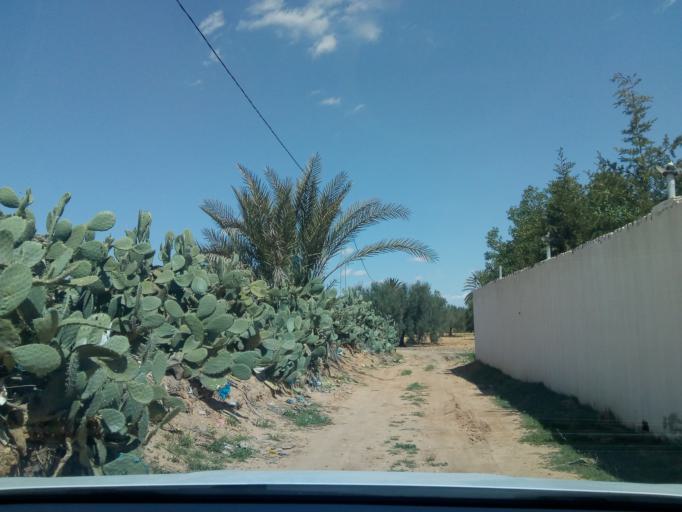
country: TN
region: Safaqis
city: Sfax
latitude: 34.7375
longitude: 10.4950
